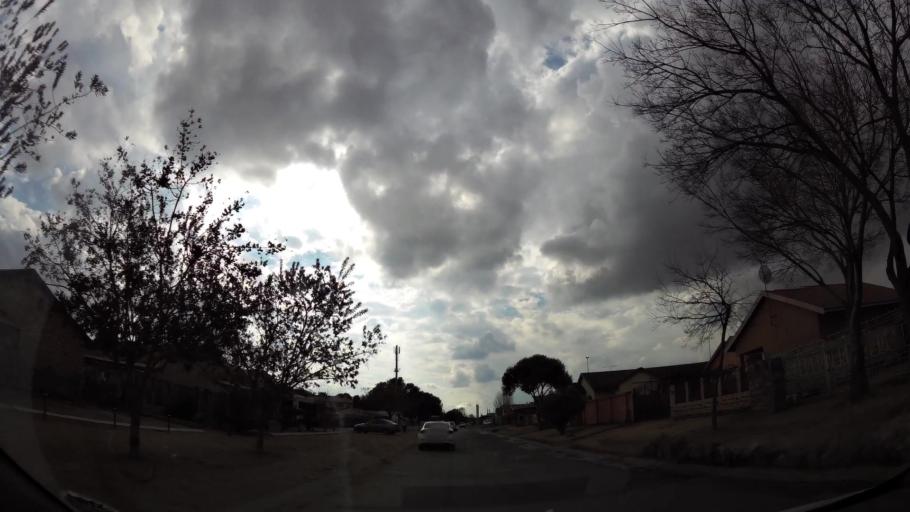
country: ZA
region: Orange Free State
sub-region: Fezile Dabi District Municipality
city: Sasolburg
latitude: -26.8458
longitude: 27.8471
